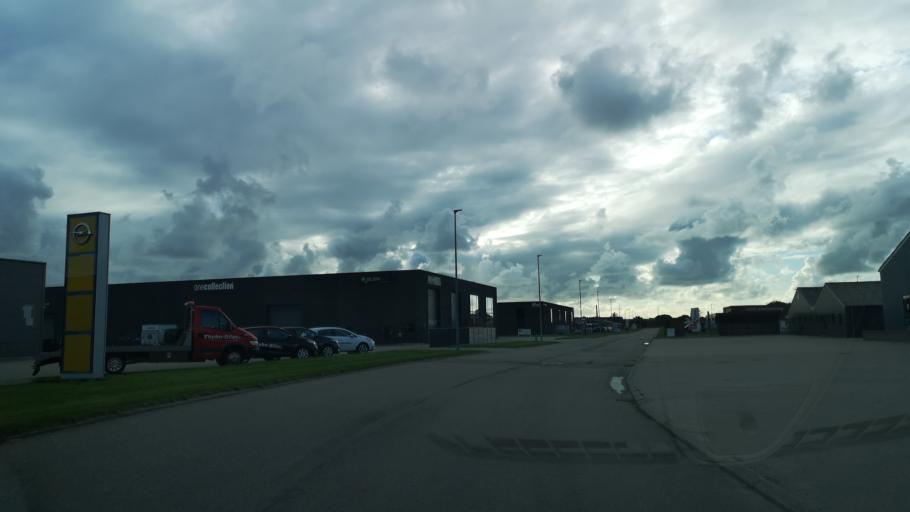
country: DK
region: Central Jutland
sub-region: Ringkobing-Skjern Kommune
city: Ringkobing
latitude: 56.0882
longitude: 8.2746
